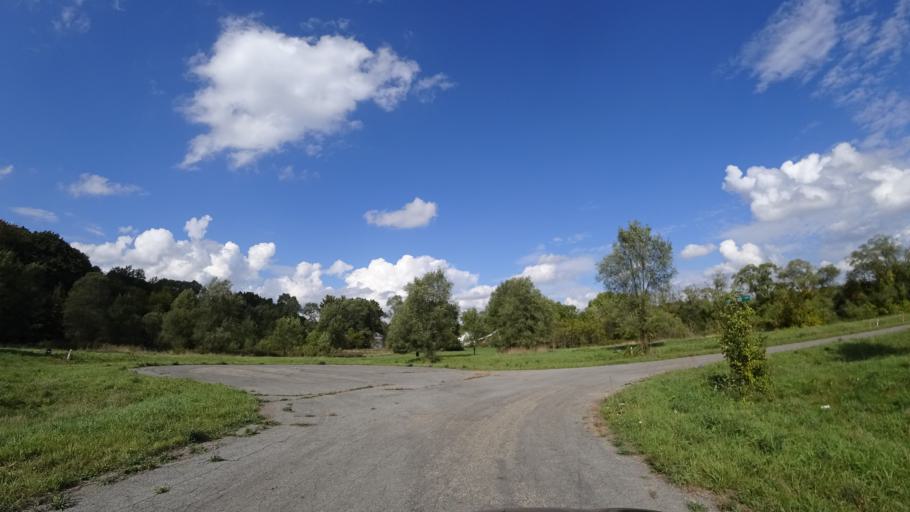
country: US
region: Michigan
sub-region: Saint Joseph County
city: Three Rivers
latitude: 41.9455
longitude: -85.6082
